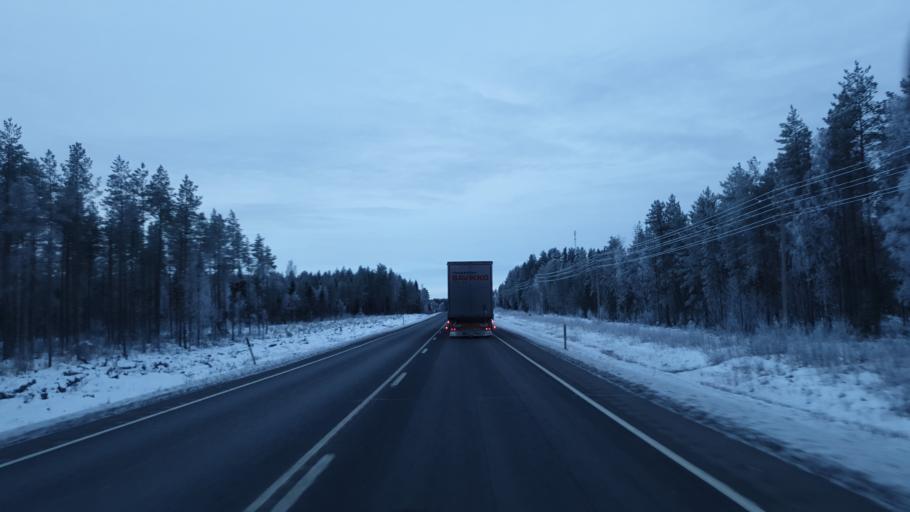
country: FI
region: Northern Ostrobothnia
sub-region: Oulunkaari
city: Ii
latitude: 65.3590
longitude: 25.3724
